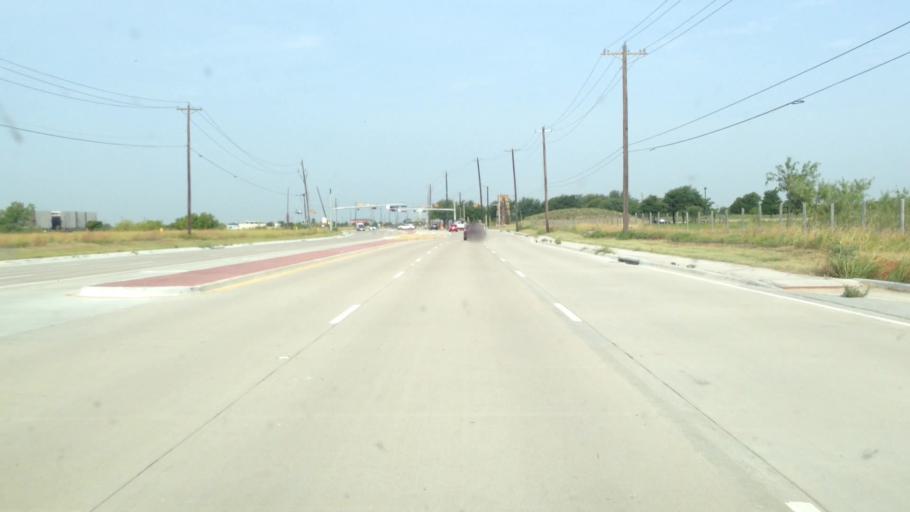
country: US
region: Texas
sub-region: Denton County
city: The Colony
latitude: 33.0449
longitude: -96.8711
